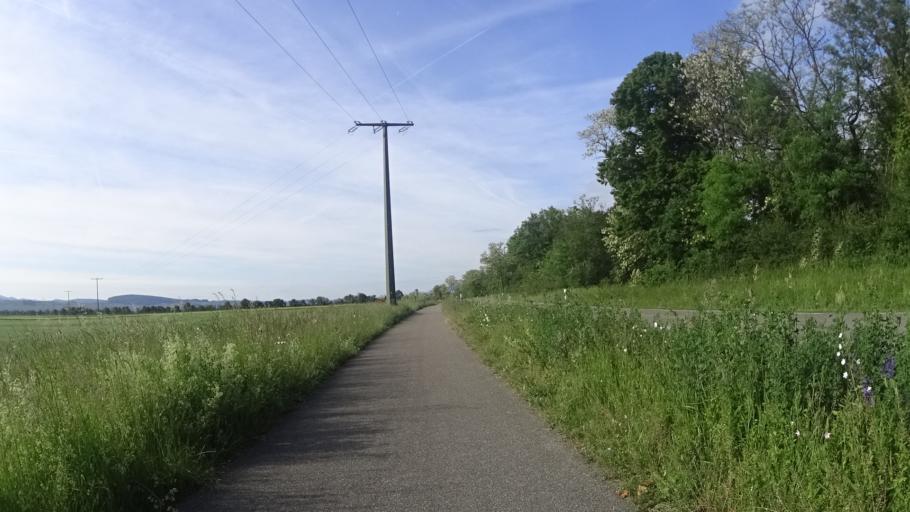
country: DE
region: Baden-Wuerttemberg
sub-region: Freiburg Region
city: Neuenburg am Rhein
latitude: 47.8358
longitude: 7.5750
